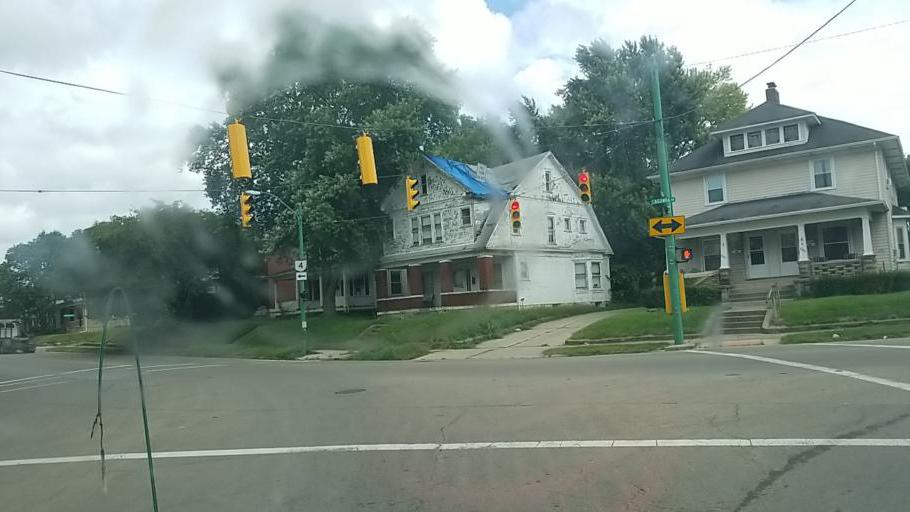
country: US
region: Ohio
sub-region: Clark County
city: Springfield
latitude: 39.9250
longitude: -83.7959
